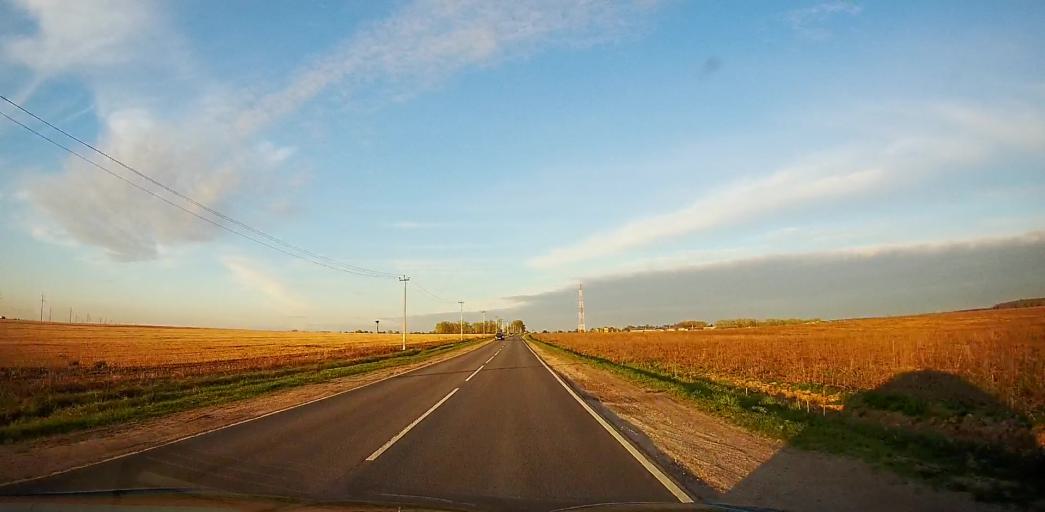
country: RU
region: Moskovskaya
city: Raduzhnyy
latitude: 55.2097
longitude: 38.6503
